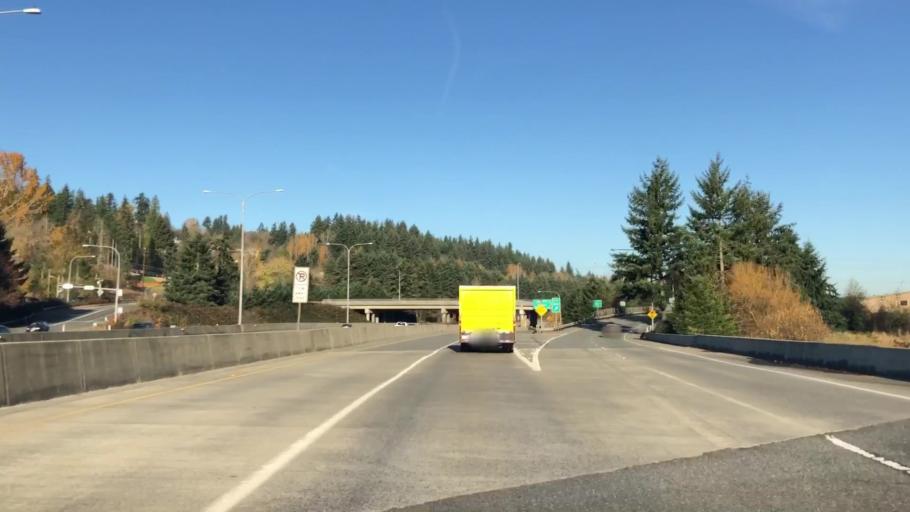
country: US
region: Washington
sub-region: King County
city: Bothell
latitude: 47.7667
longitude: -122.1880
